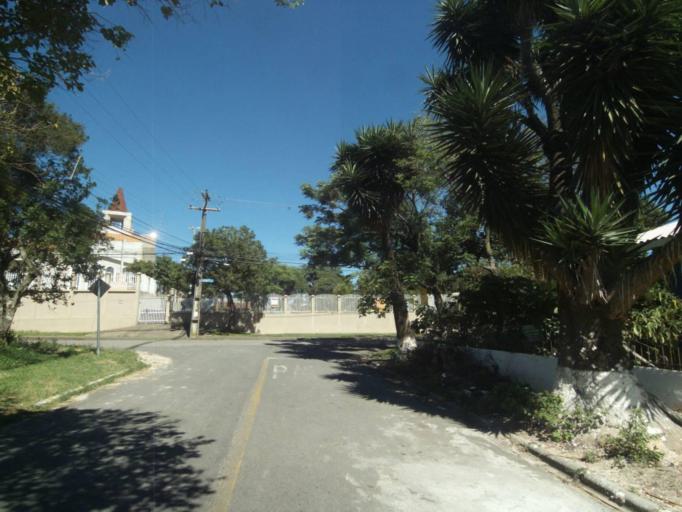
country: BR
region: Parana
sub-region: Curitiba
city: Curitiba
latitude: -25.4859
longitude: -49.3438
